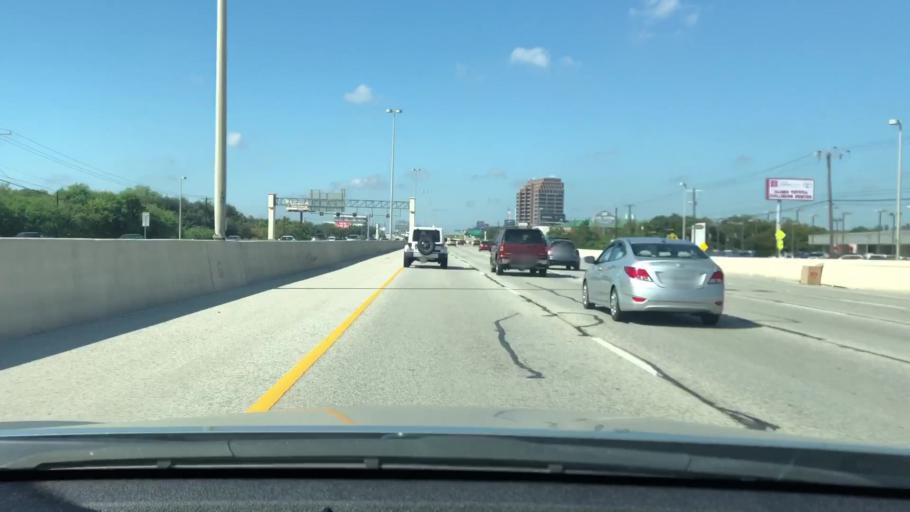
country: US
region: Texas
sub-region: Bexar County
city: Windcrest
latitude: 29.5160
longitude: -98.4274
